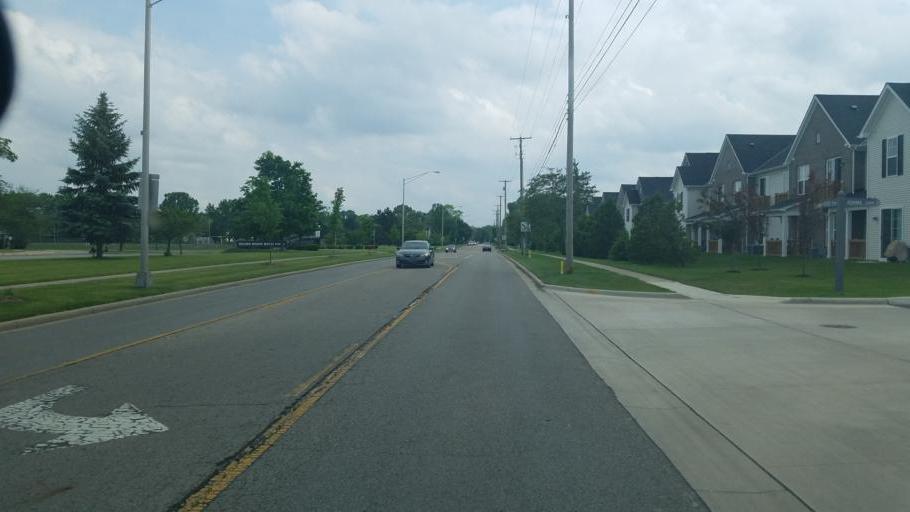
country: US
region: Ohio
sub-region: Franklin County
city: Hilliard
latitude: 40.0466
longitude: -83.1585
